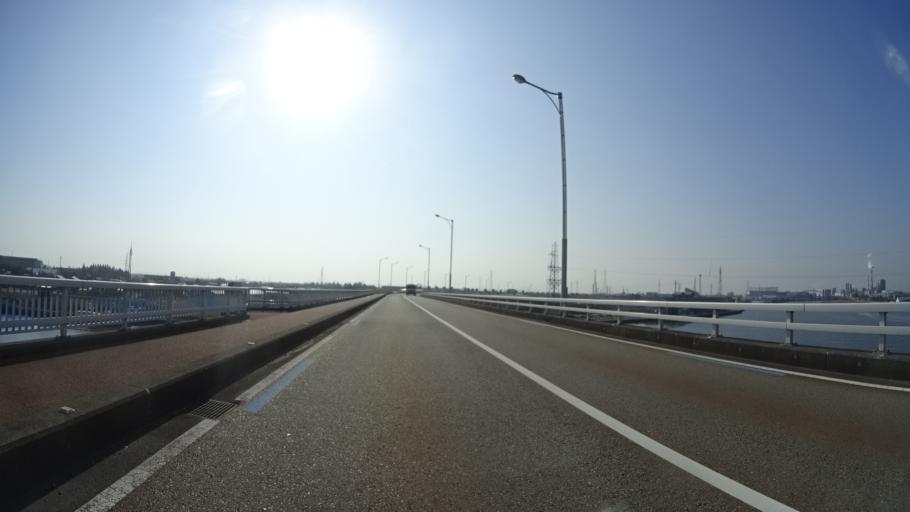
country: JP
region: Toyama
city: Nishishinminato
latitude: 36.7884
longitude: 137.0584
